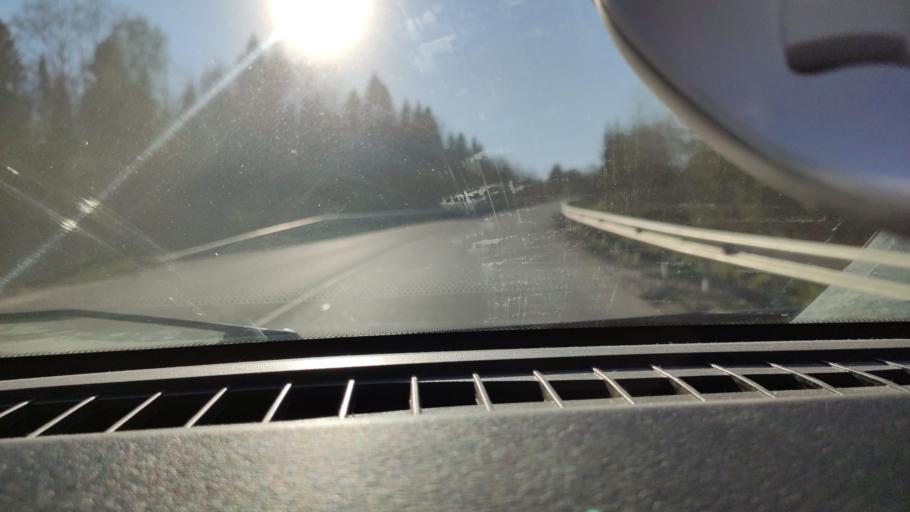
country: RU
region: Perm
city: Novyye Lyady
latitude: 58.1209
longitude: 56.4526
